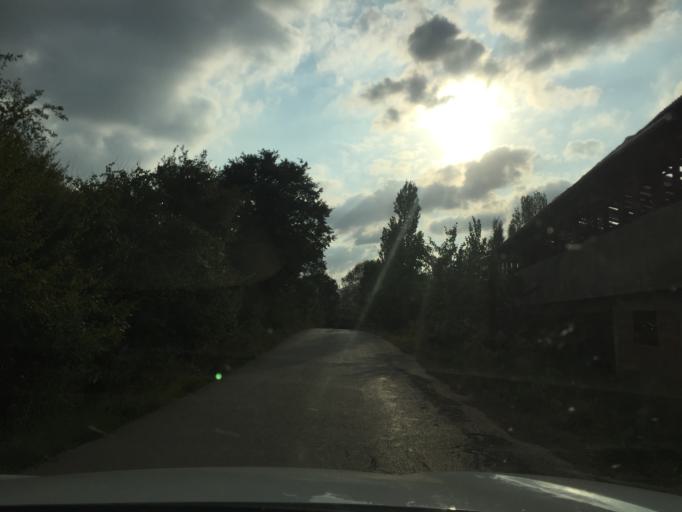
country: TR
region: Balikesir
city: Gonen
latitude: 40.0522
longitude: 27.5899
